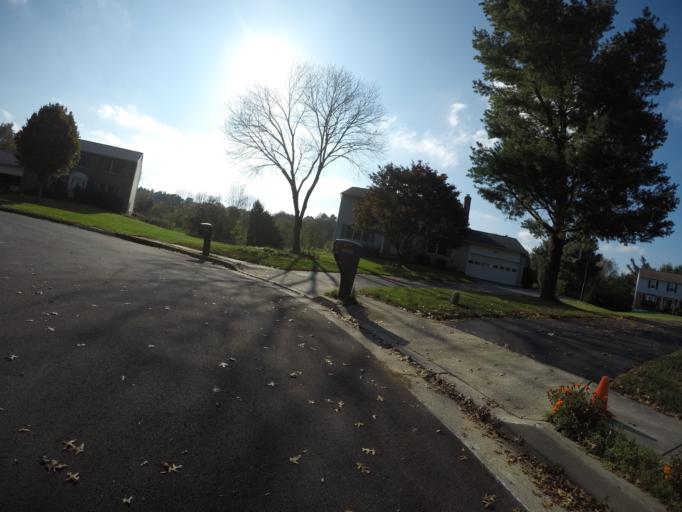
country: US
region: Maryland
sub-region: Howard County
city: Columbia
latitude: 39.2747
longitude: -76.8501
